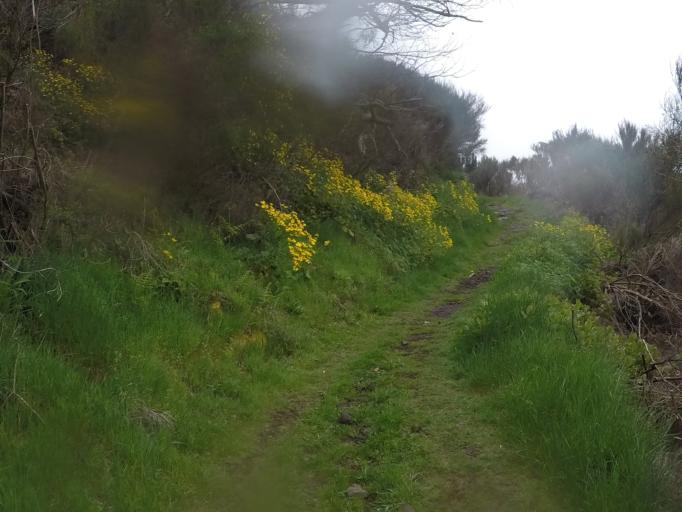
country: PT
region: Madeira
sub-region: Camara de Lobos
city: Curral das Freiras
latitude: 32.7273
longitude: -16.9853
